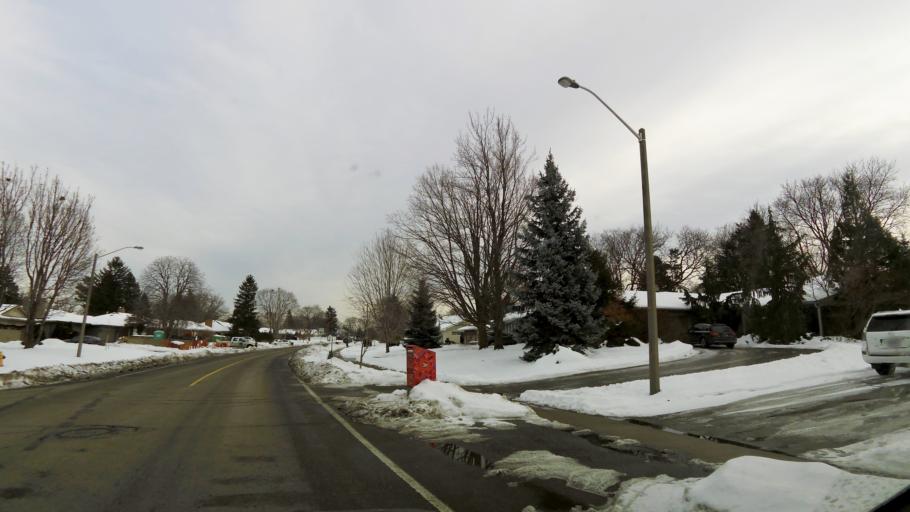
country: CA
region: Ontario
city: Etobicoke
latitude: 43.6737
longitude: -79.5461
